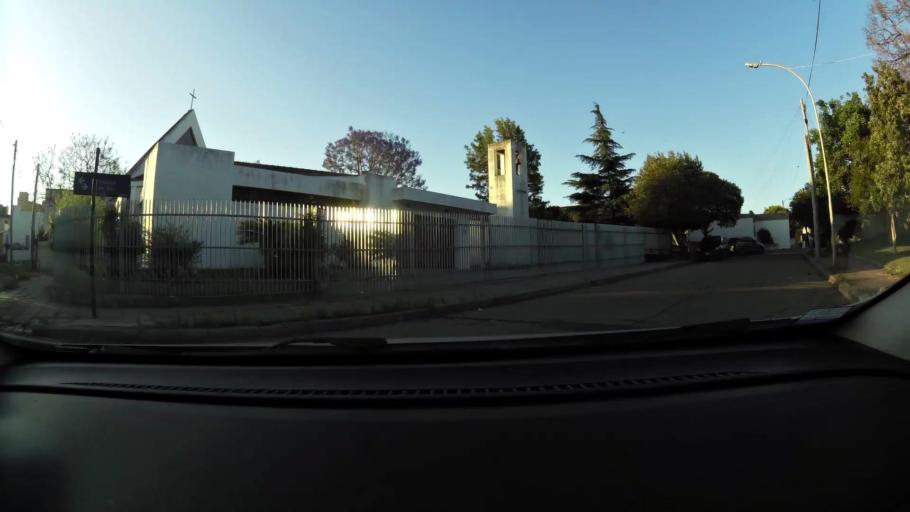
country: AR
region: Cordoba
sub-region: Departamento de Capital
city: Cordoba
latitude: -31.3803
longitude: -64.2118
